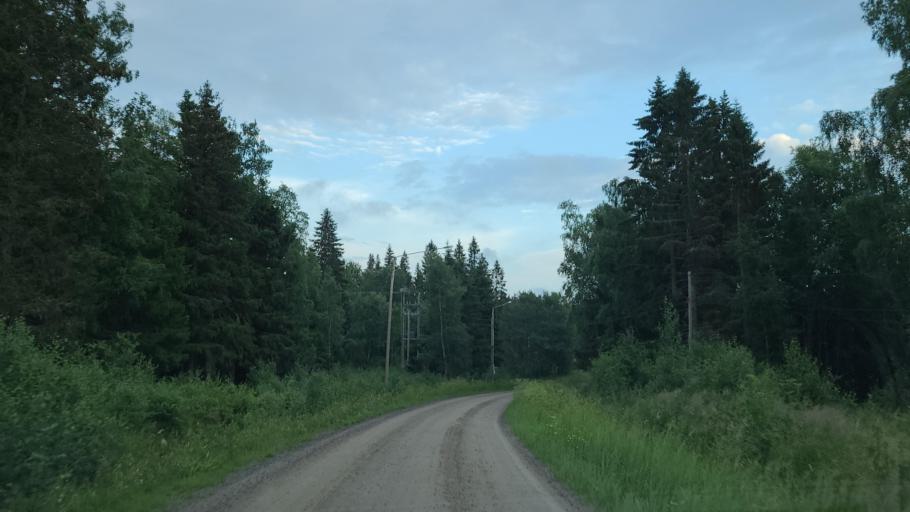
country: FI
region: Ostrobothnia
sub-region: Vaasa
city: Replot
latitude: 63.3143
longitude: 21.1599
